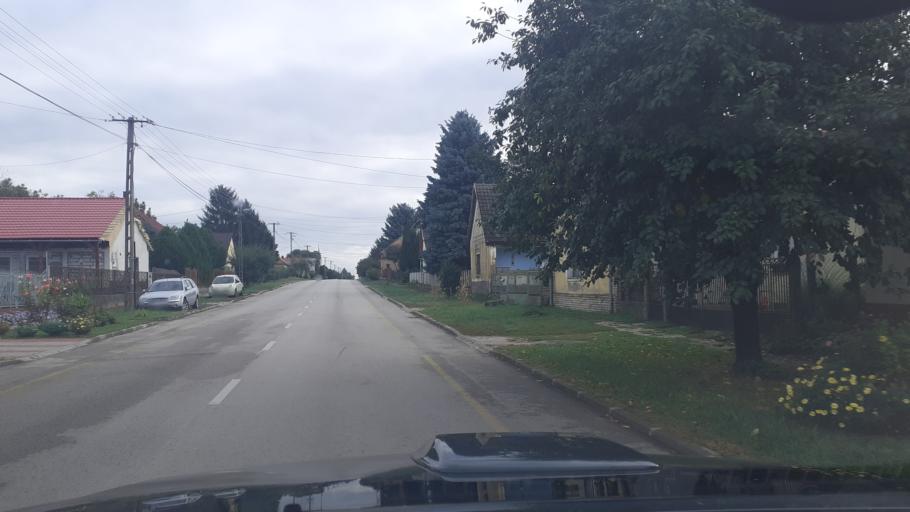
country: HU
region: Fejer
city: Baracs
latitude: 46.9085
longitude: 18.8617
